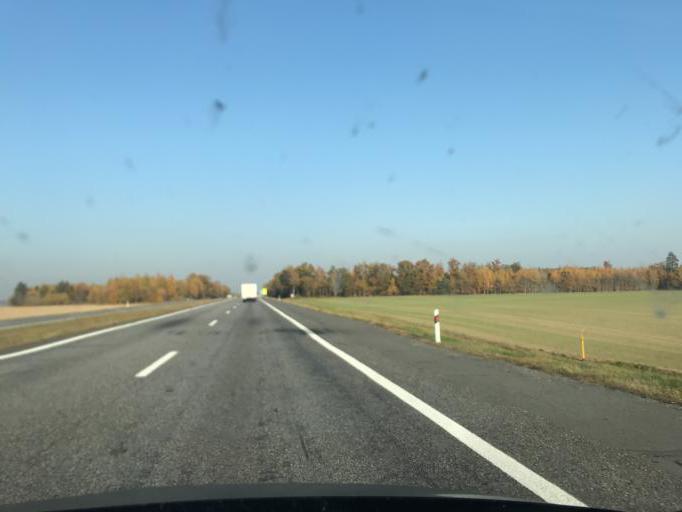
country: BY
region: Minsk
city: Haradzyeya
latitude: 53.3738
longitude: 26.4977
